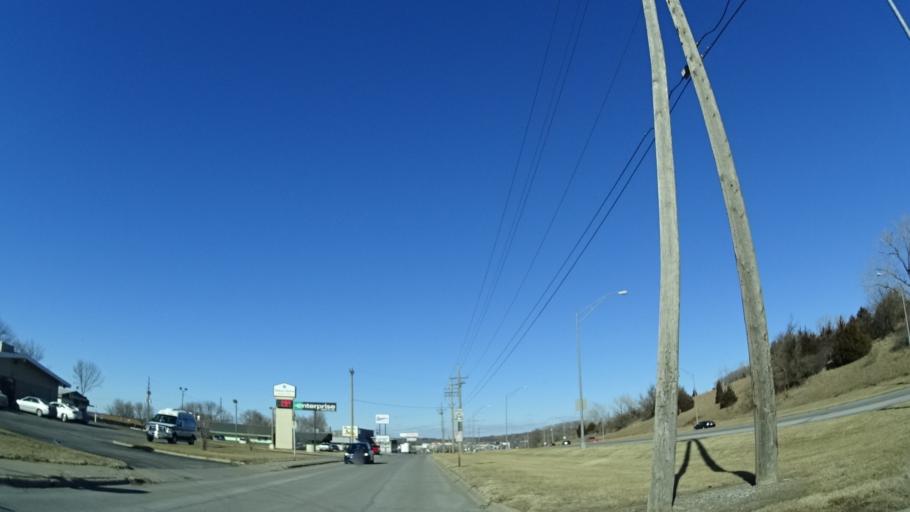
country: US
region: Nebraska
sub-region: Sarpy County
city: Offutt Air Force Base
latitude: 41.1498
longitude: -95.9279
